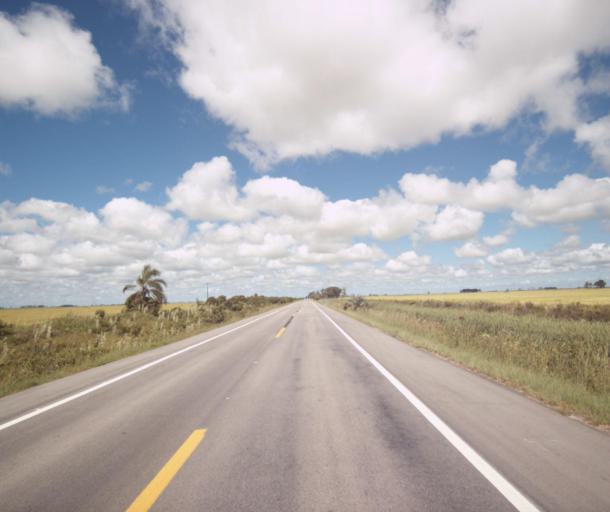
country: BR
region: Rio Grande do Sul
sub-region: Rio Grande
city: Rio Grande
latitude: -32.1576
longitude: -52.3987
